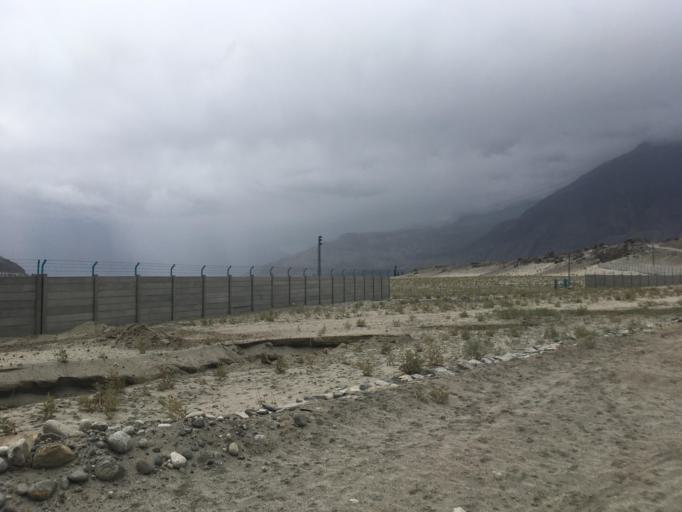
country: PK
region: Gilgit-Baltistan
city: Skardu
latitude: 35.3162
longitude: 75.6574
